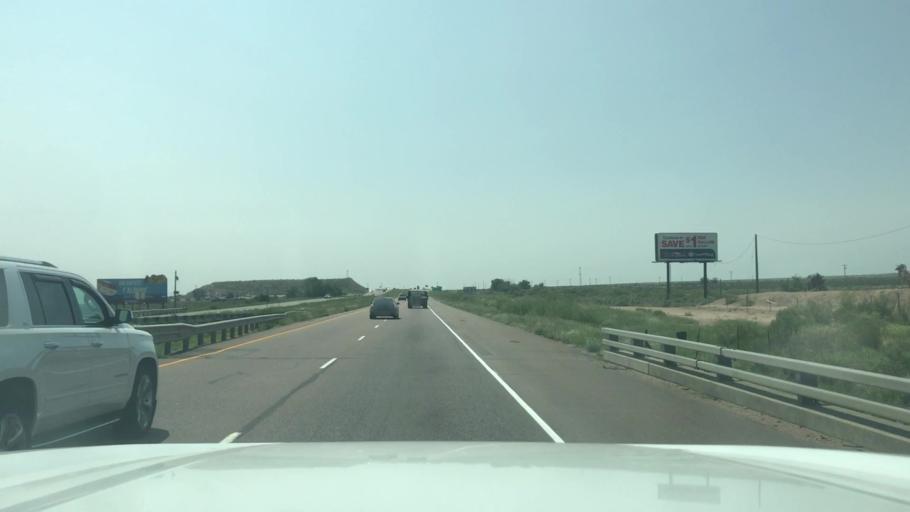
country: US
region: Colorado
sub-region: Pueblo County
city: Pueblo West
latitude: 38.4101
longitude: -104.6139
